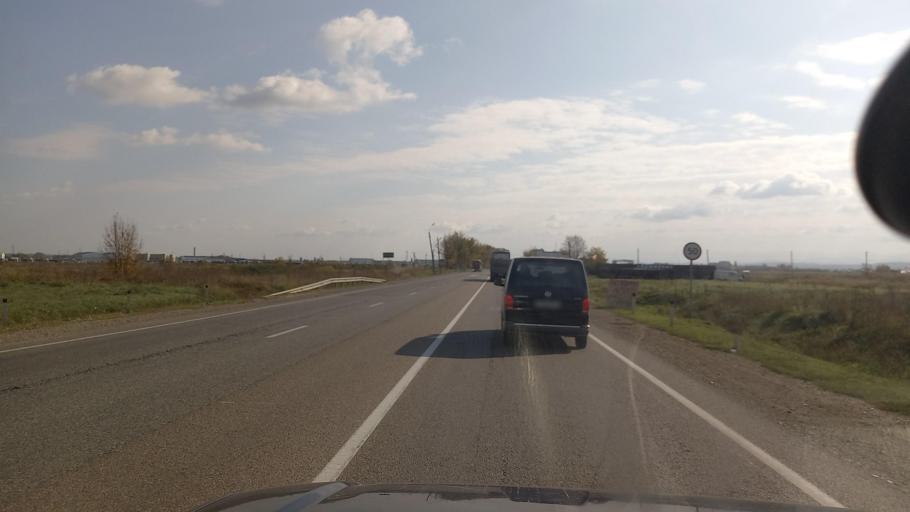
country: RU
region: Krasnodarskiy
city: Abinsk
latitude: 44.8725
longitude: 38.1216
